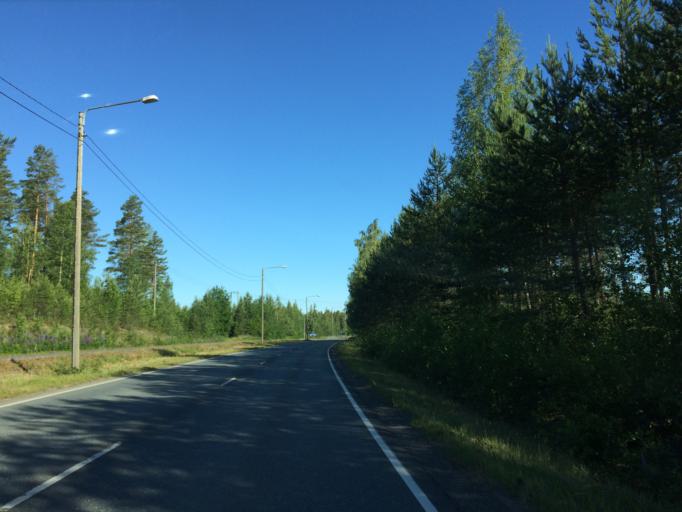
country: FI
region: Haeme
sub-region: Haemeenlinna
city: Haemeenlinna
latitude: 60.9618
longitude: 24.4531
